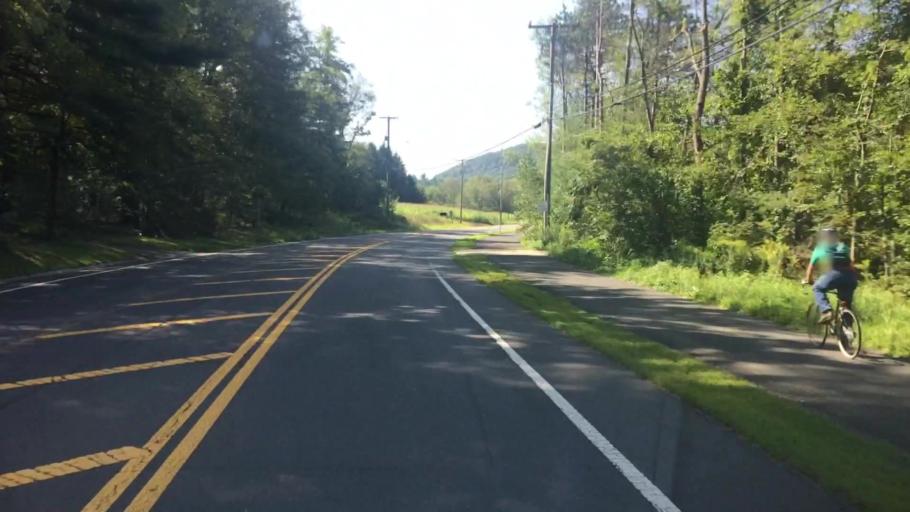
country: US
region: Massachusetts
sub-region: Hampshire County
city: South Amherst
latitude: 42.3223
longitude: -72.5250
